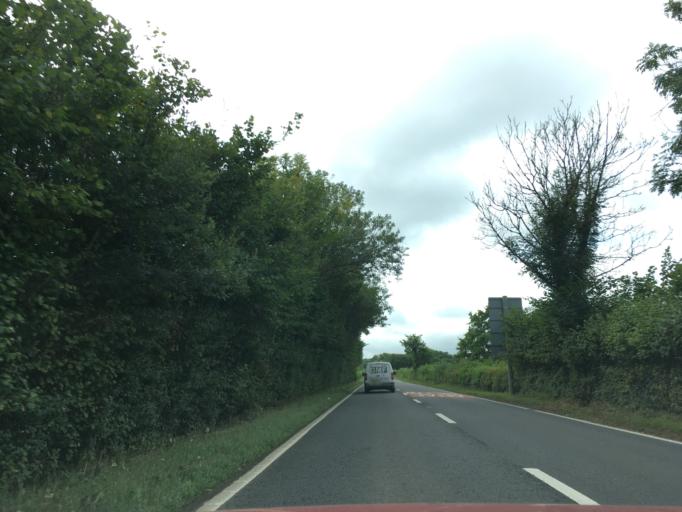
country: GB
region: Wales
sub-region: Carmarthenshire
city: Llangathen
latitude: 51.8789
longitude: -4.0838
